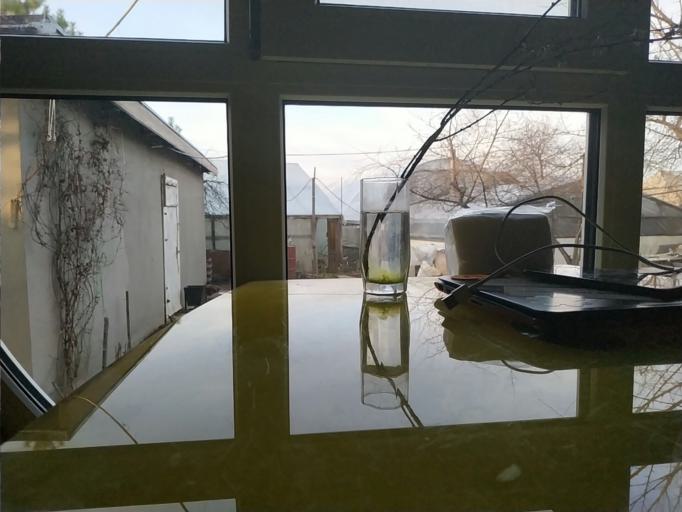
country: RU
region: Republic of Karelia
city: Suoyarvi
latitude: 62.3056
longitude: 32.0700
